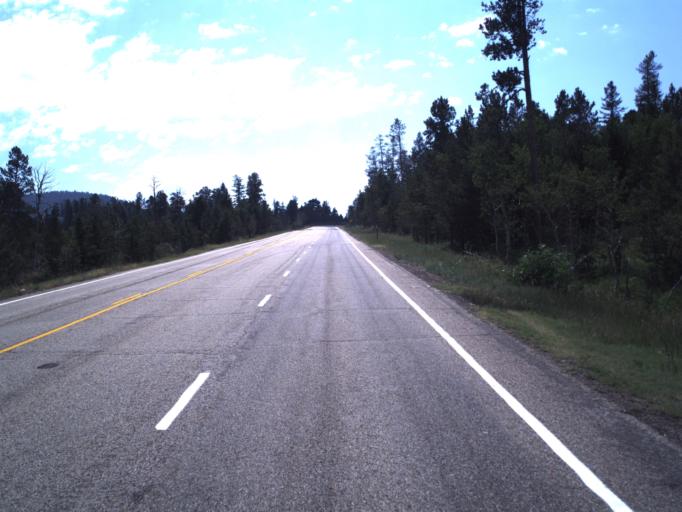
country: US
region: Utah
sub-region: Daggett County
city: Manila
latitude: 40.8582
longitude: -109.4662
